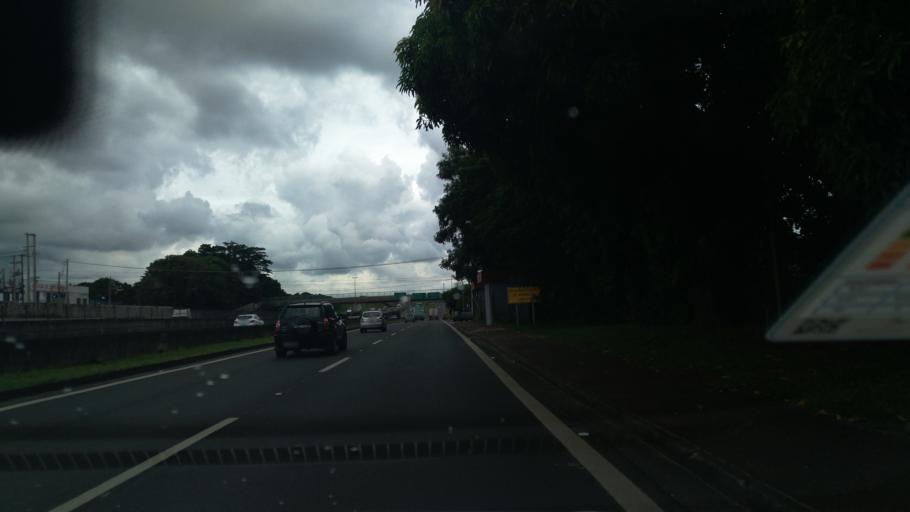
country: BR
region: Sao Paulo
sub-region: Campinas
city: Campinas
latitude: -22.8904
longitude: -47.1127
